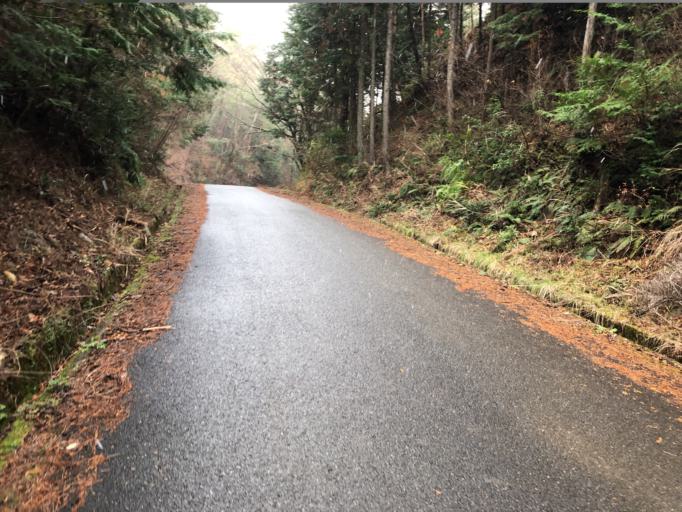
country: JP
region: Kyoto
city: Kameoka
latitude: 35.0599
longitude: 135.4965
